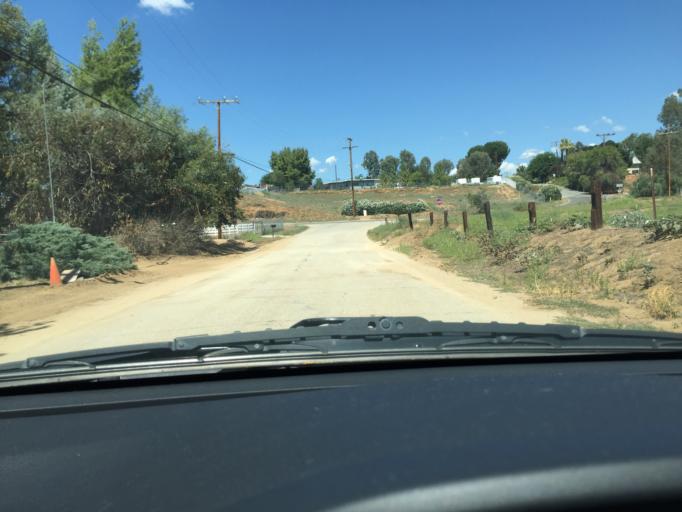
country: US
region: California
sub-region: Riverside County
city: Calimesa
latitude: 33.9984
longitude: -117.0261
